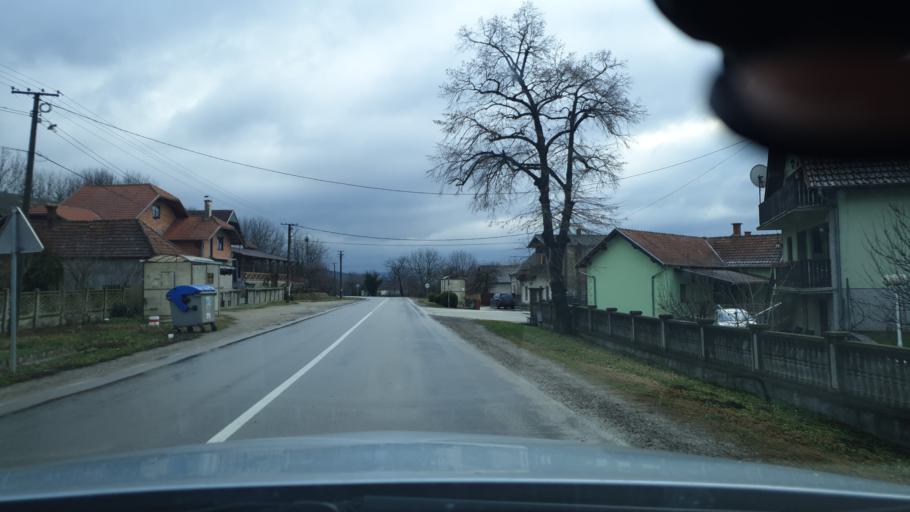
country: RS
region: Central Serbia
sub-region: Branicevski Okrug
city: Petrovac
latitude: 44.4351
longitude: 21.3506
